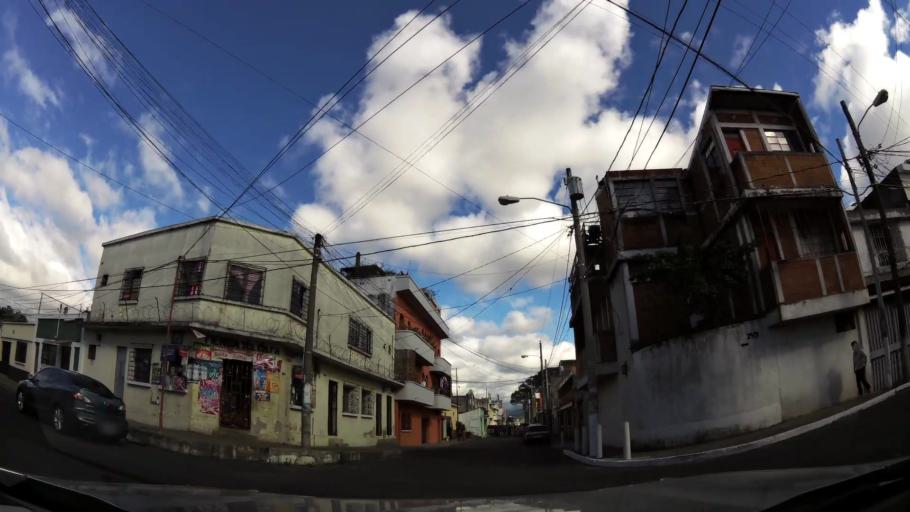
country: GT
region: Guatemala
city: Guatemala City
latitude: 14.6203
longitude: -90.5114
